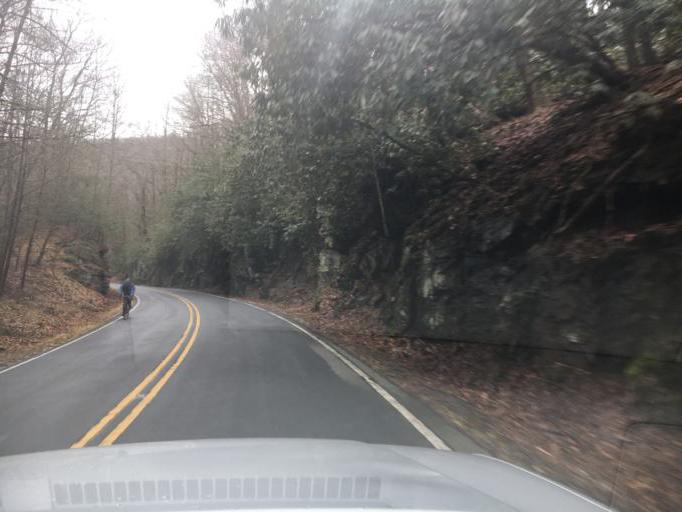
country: US
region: North Carolina
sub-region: Transylvania County
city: Brevard
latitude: 35.2838
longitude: -82.7555
